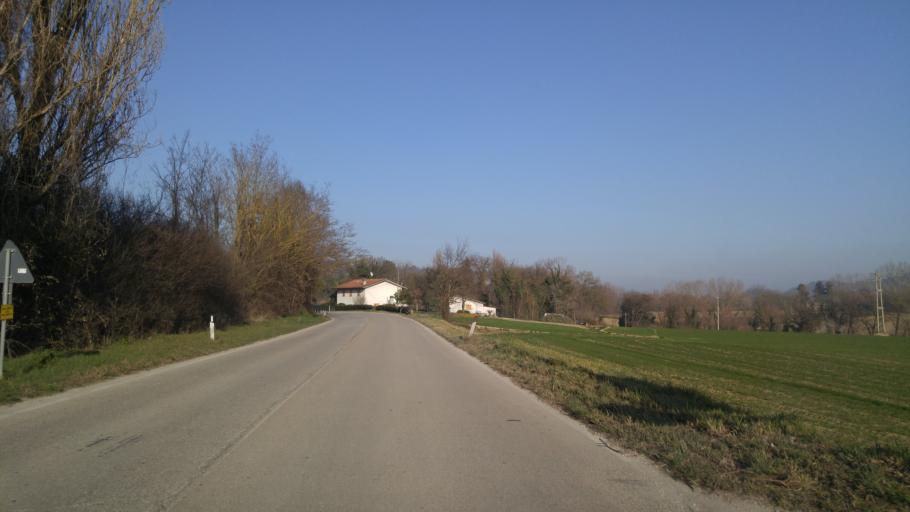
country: IT
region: The Marches
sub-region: Provincia di Pesaro e Urbino
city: Fenile
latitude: 43.8338
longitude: 12.9297
